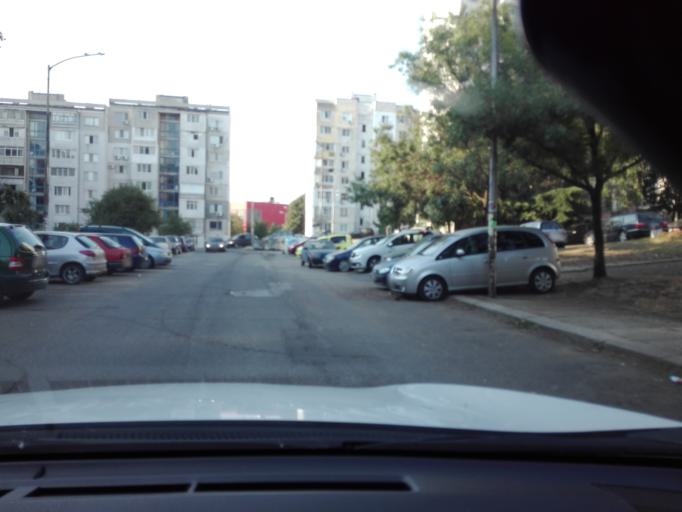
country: BG
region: Burgas
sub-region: Obshtina Burgas
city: Burgas
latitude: 42.4632
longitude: 27.4154
